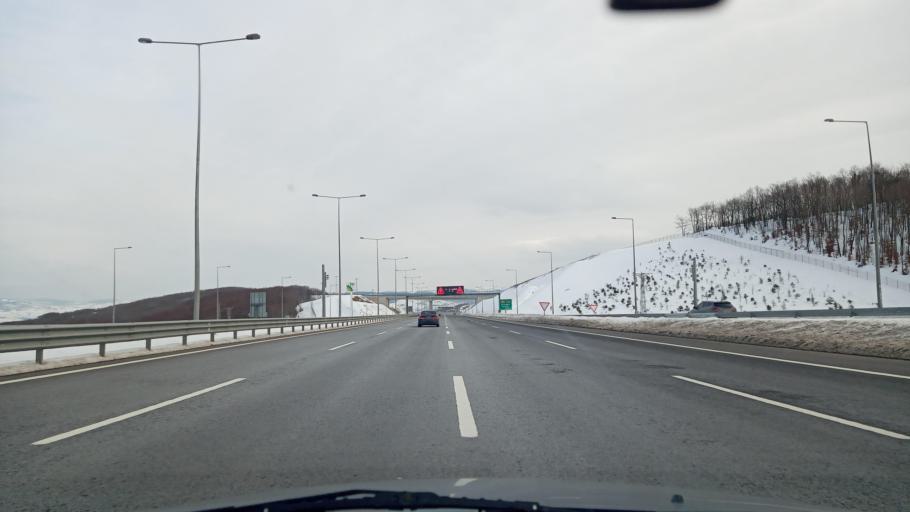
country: TR
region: Kocaeli
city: Korfez
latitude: 40.8894
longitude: 29.7179
